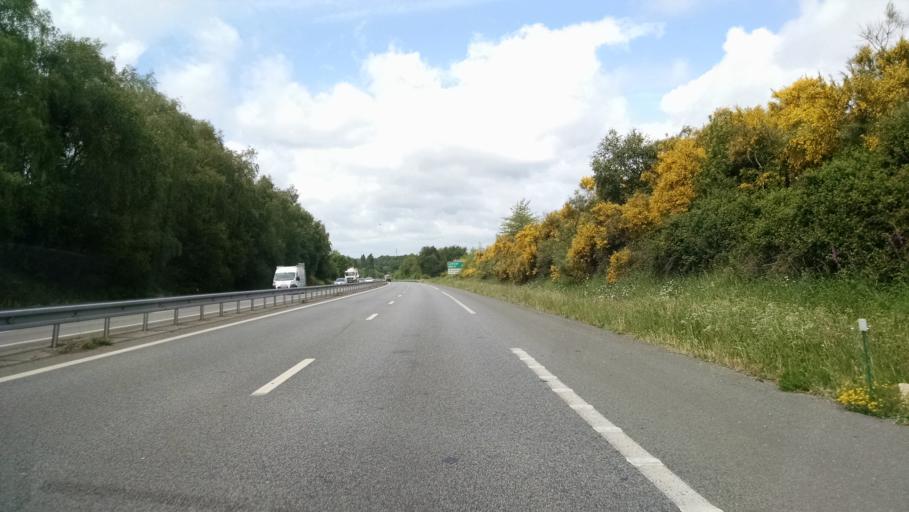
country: FR
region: Brittany
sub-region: Departement du Morbihan
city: Landevant
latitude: 47.7621
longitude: -3.1396
